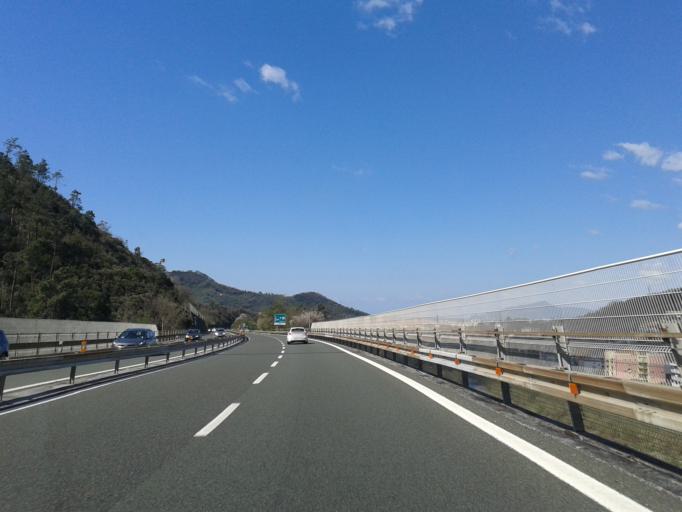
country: IT
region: Liguria
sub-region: Provincia di Genova
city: Casarza Ligure
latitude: 44.2689
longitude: 9.4418
